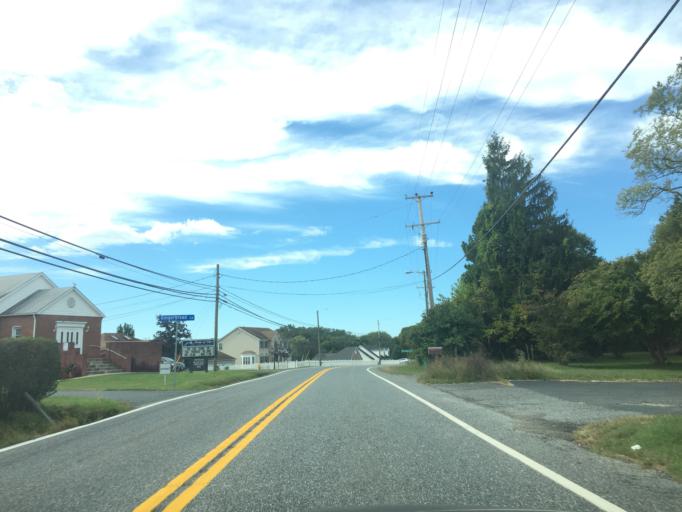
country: US
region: Maryland
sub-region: Harford County
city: Joppatowne
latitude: 39.4336
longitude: -76.3589
